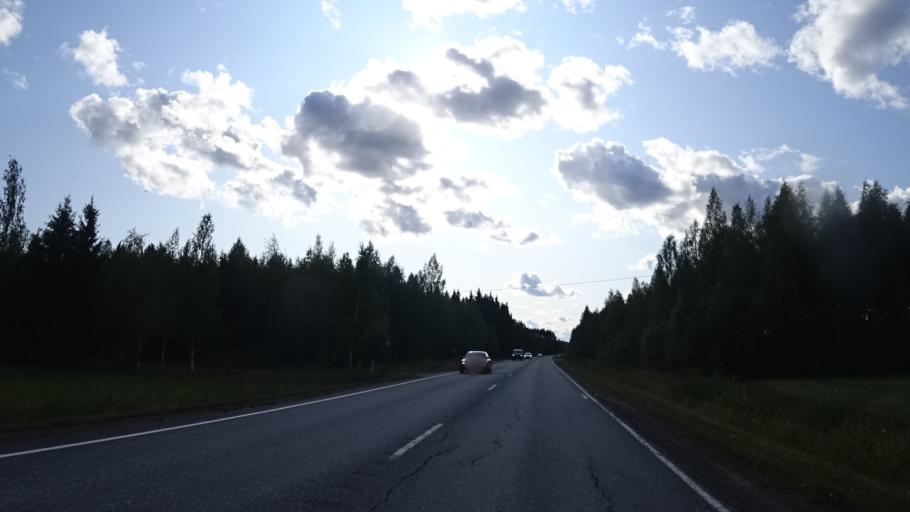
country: FI
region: North Karelia
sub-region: Keski-Karjala
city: Kitee
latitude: 62.0922
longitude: 30.0463
